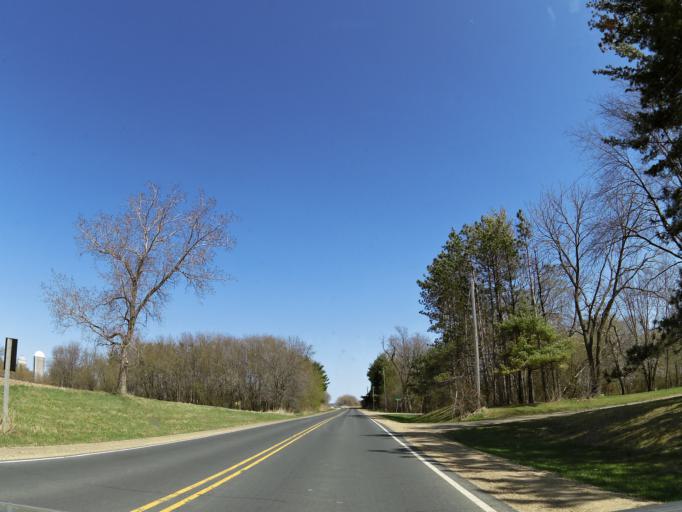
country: US
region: Wisconsin
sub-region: Saint Croix County
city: Roberts
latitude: 44.9418
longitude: -92.5618
